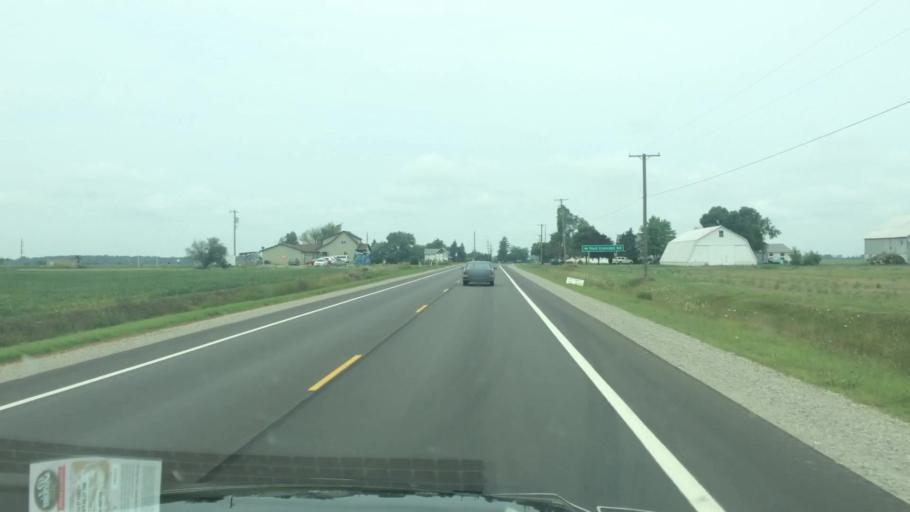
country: US
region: Michigan
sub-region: Huron County
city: Bad Axe
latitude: 44.0011
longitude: -83.0078
